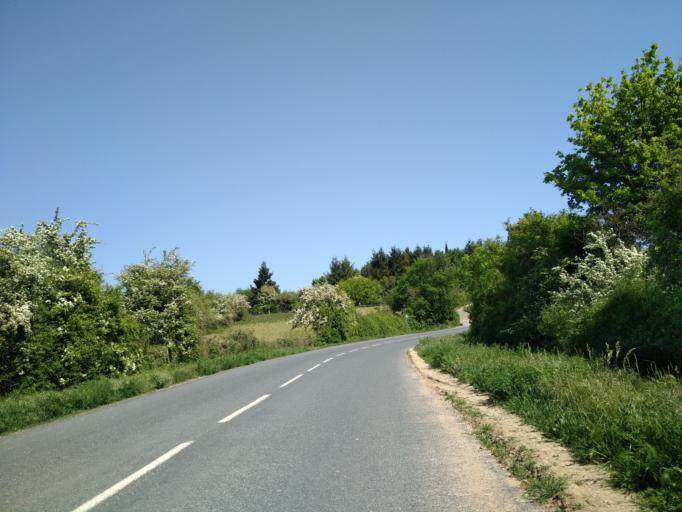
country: FR
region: Rhone-Alpes
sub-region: Departement du Rhone
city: Fontaines-sur-Saone
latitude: 45.8252
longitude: 4.8171
